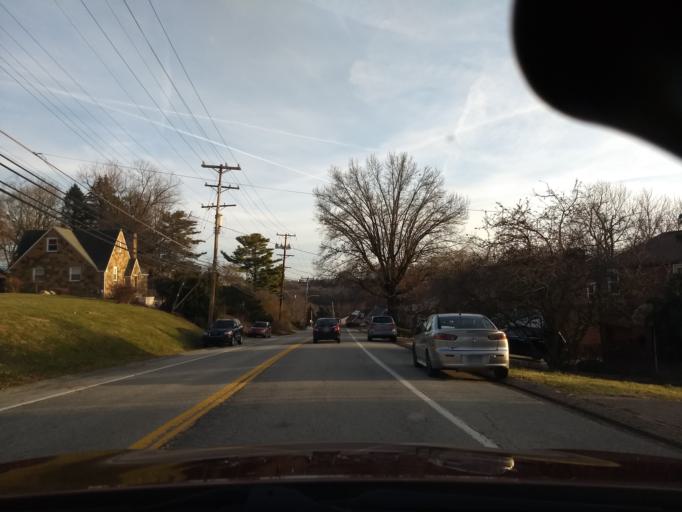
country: US
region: Pennsylvania
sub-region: Allegheny County
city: Brentwood
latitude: 40.3628
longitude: -79.9636
